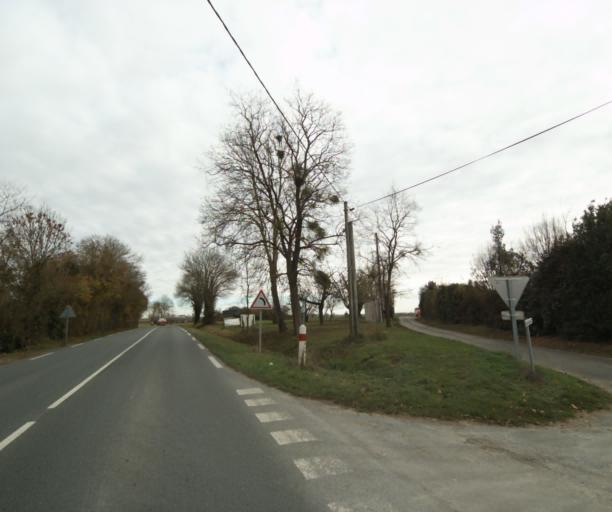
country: FR
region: Poitou-Charentes
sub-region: Departement de la Charente-Maritime
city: Corme-Royal
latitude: 45.7386
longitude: -0.8250
